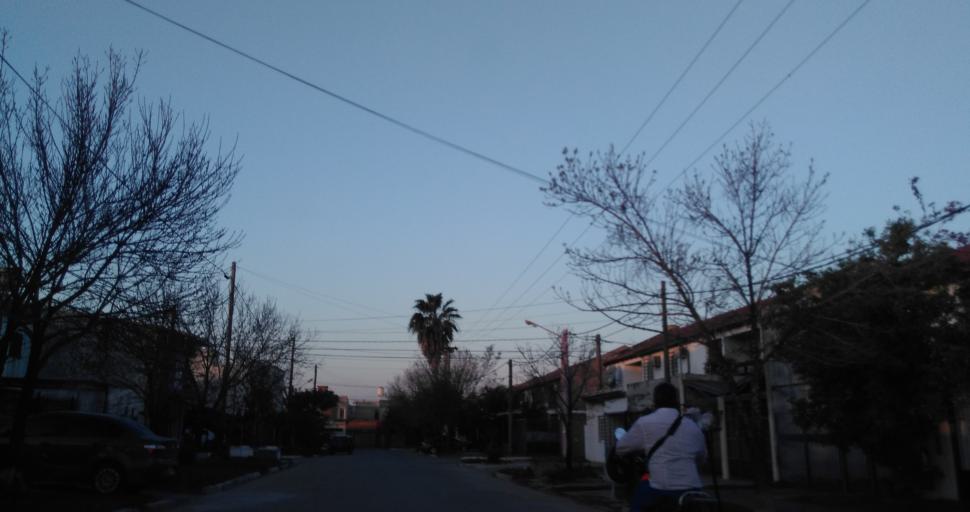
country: AR
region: Chaco
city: Resistencia
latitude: -27.4408
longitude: -58.9644
